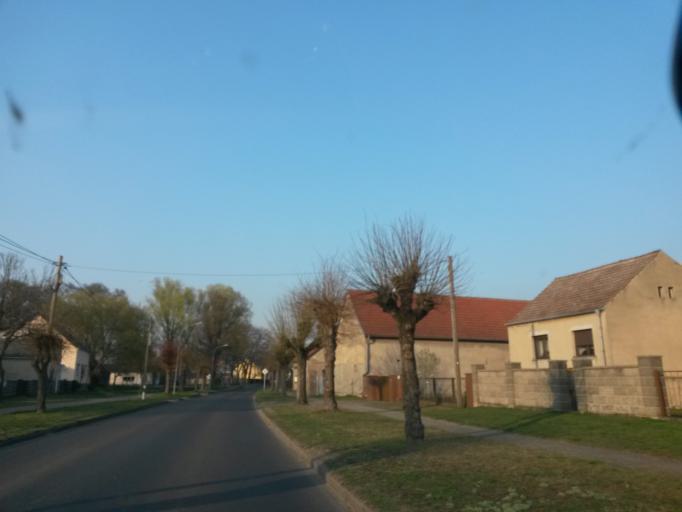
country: DE
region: Brandenburg
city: Rehfelde
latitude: 52.5016
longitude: 13.9233
